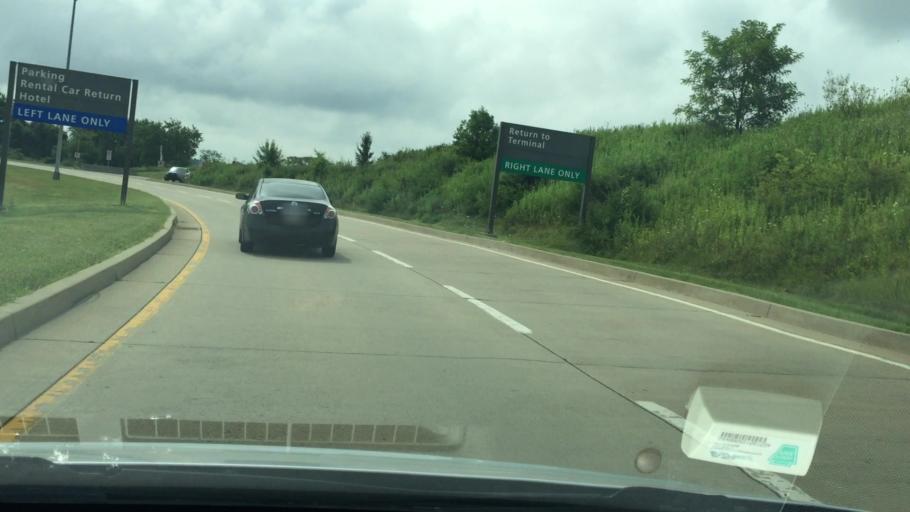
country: US
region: Pennsylvania
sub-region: Allegheny County
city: Imperial
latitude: 40.4908
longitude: -80.2654
